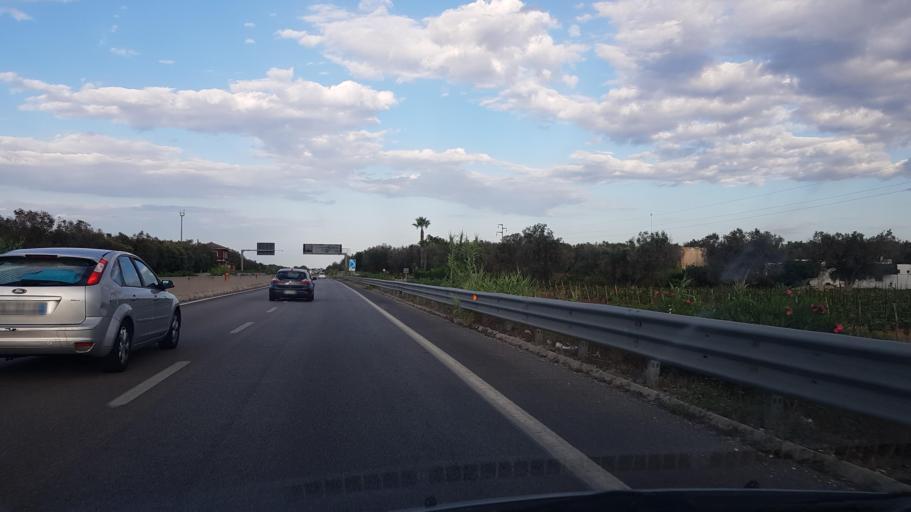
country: IT
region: Apulia
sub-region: Provincia di Brindisi
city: Latiano
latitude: 40.5421
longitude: 17.6748
